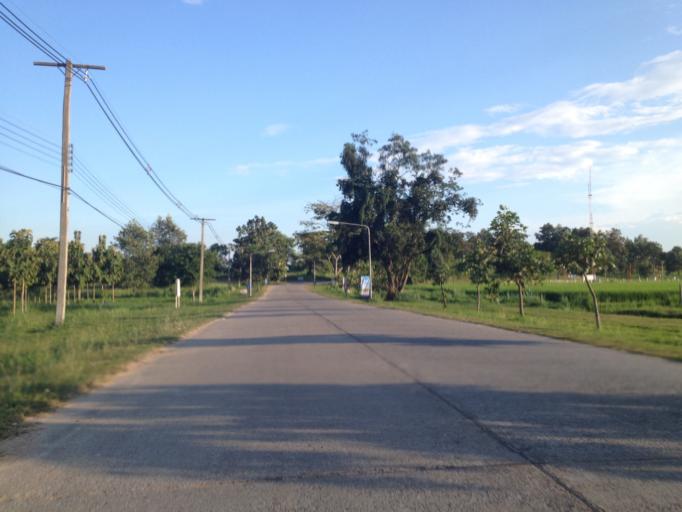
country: TH
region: Chiang Mai
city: Chiang Mai
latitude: 18.7630
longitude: 98.9315
